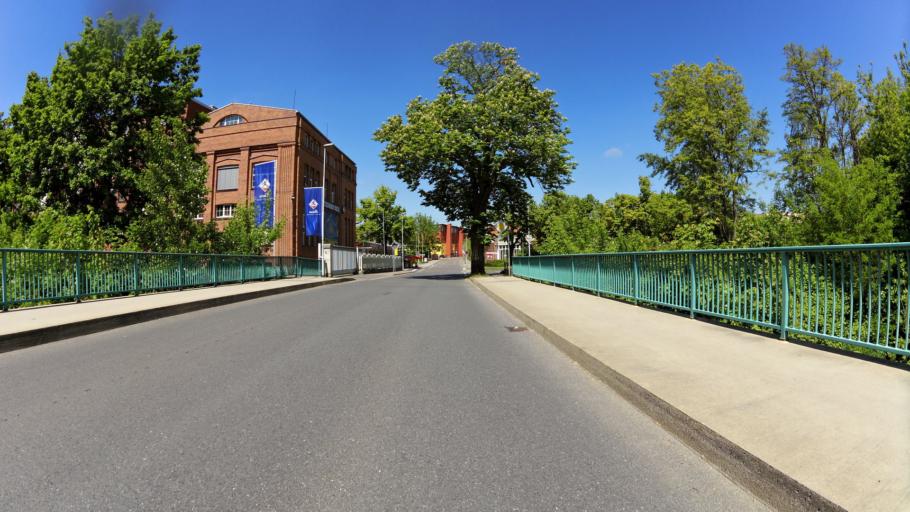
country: DE
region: Saxony
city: Riesa
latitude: 51.3171
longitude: 13.2627
